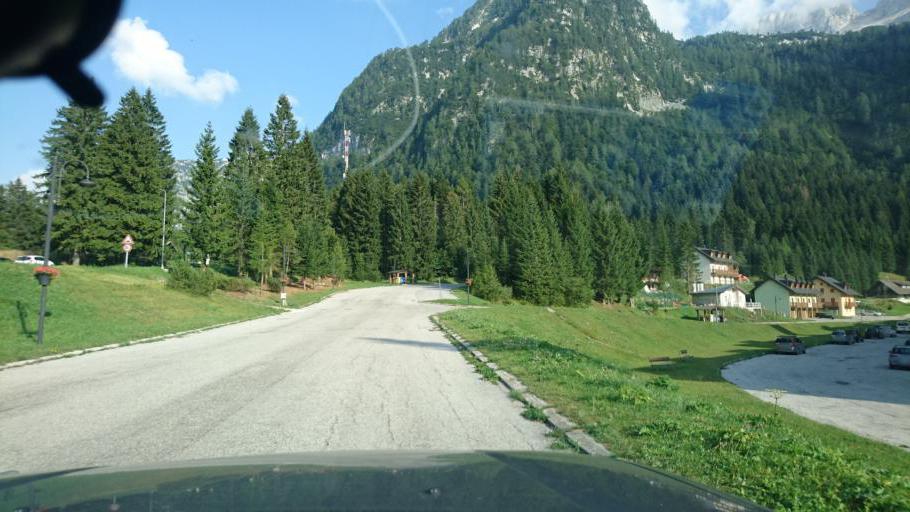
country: SI
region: Bovec
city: Bovec
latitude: 46.3907
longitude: 13.4746
